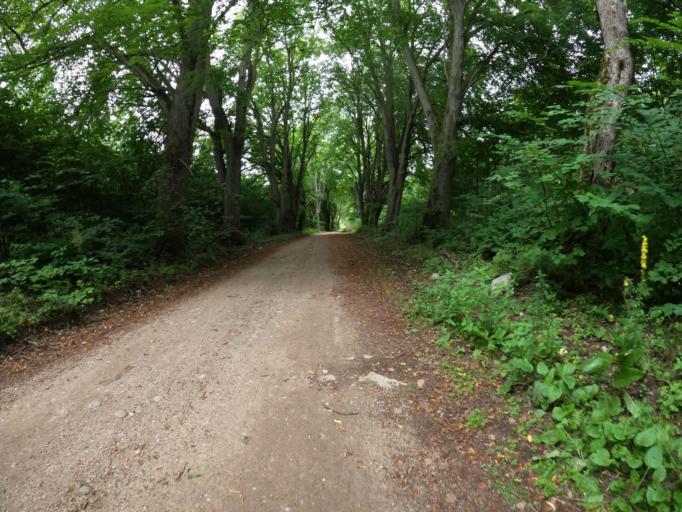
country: PL
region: West Pomeranian Voivodeship
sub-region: Powiat bialogardzki
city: Tychowo
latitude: 53.9878
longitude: 16.3827
